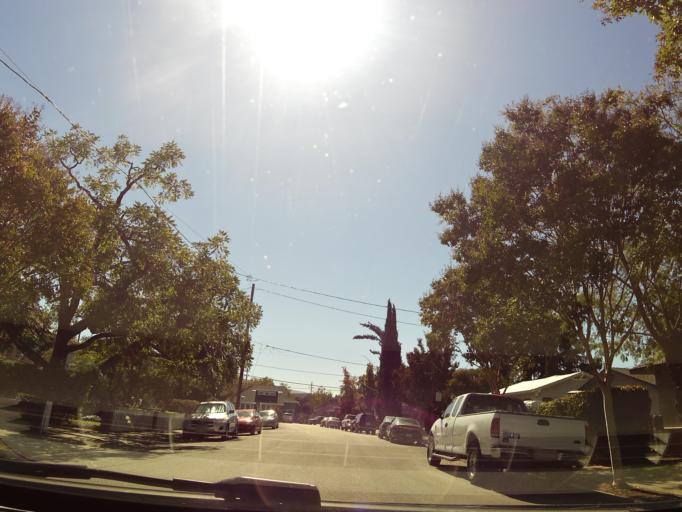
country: US
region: California
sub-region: Santa Clara County
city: Campbell
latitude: 37.2838
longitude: -121.9457
